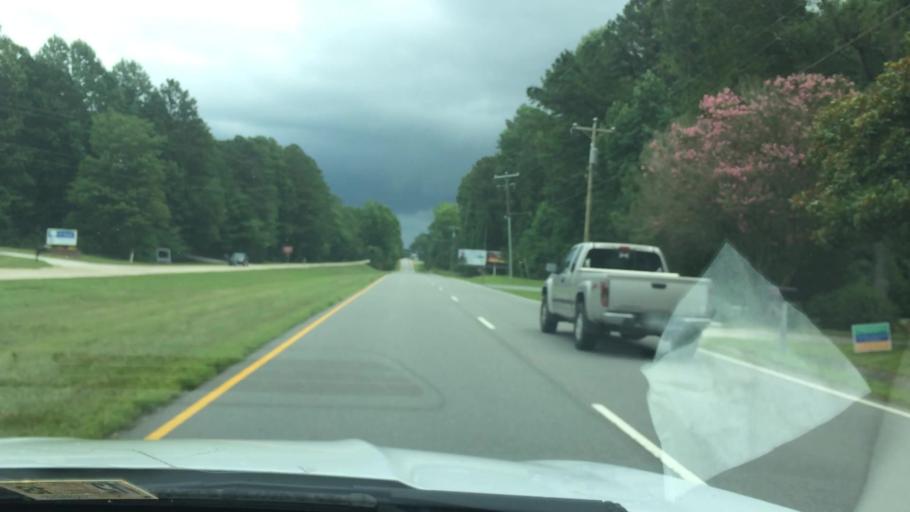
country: US
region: Virginia
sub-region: King William County
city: West Point
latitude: 37.4037
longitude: -76.8336
